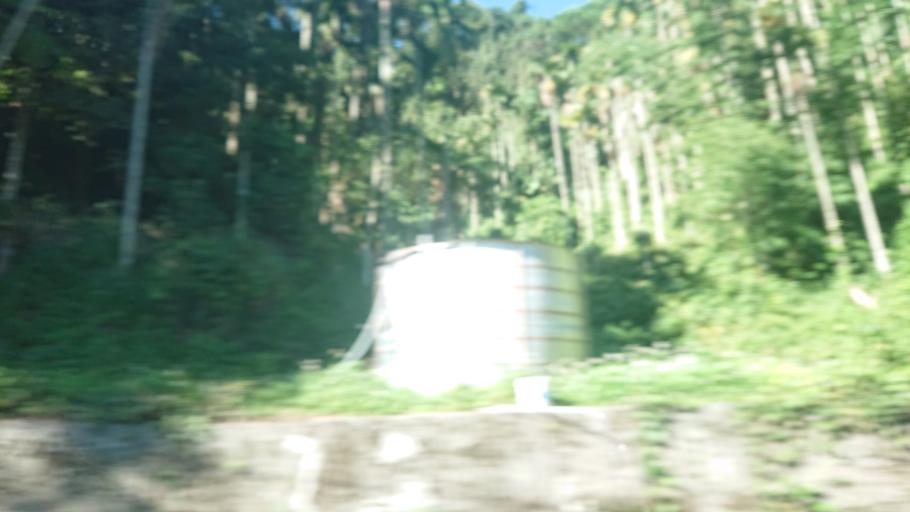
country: TW
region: Taiwan
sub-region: Chiayi
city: Jiayi Shi
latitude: 23.5310
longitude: 120.6445
